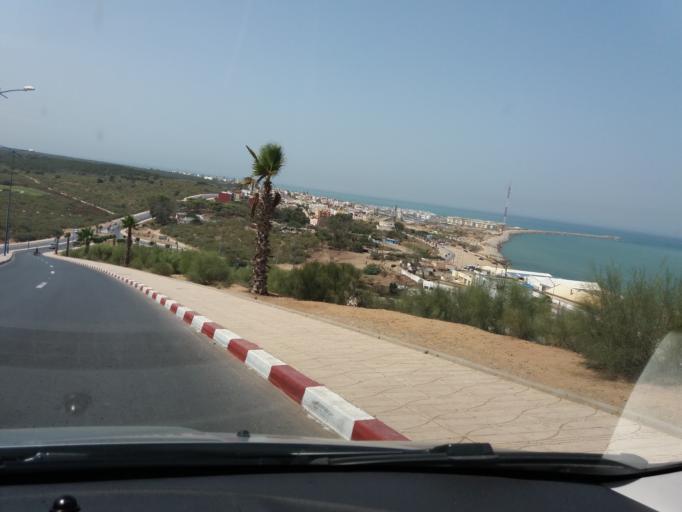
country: MA
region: Gharb-Chrarda-Beni Hssen
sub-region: Kenitra Province
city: Kenitra
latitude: 34.2623
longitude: -6.6604
